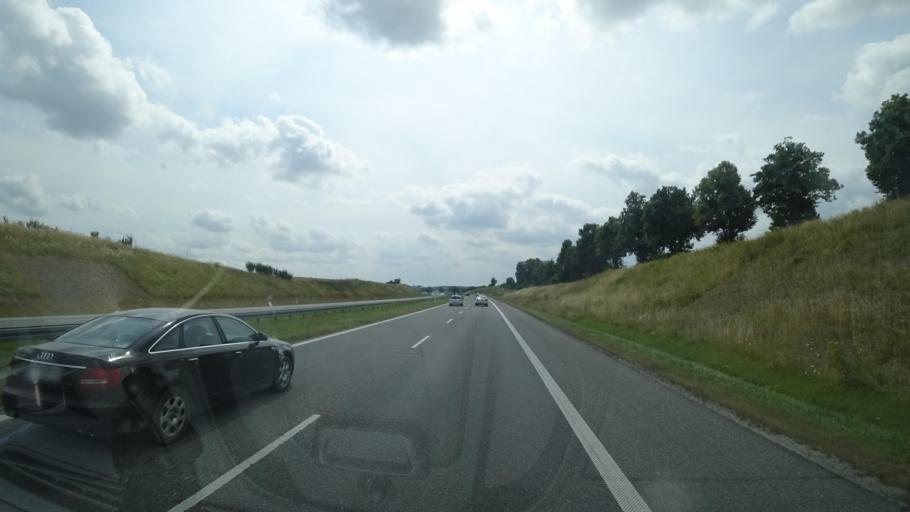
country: PL
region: Warmian-Masurian Voivodeship
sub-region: Powiat ostrodzki
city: Maldyty
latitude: 53.9558
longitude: 19.6961
